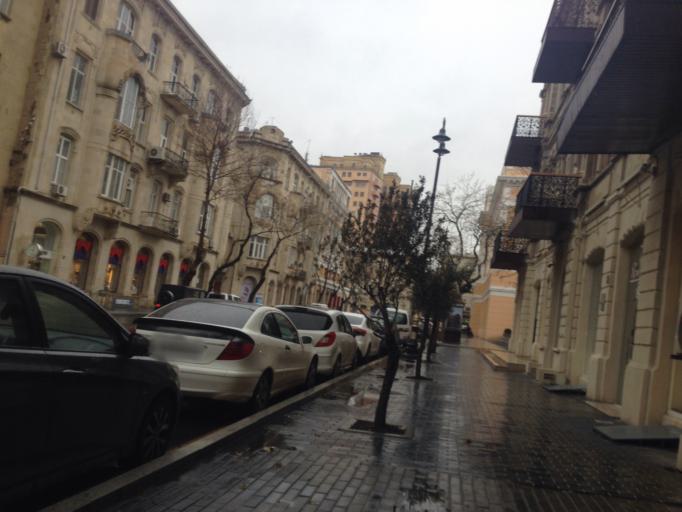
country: AZ
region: Baki
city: Baku
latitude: 40.3756
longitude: 49.8450
